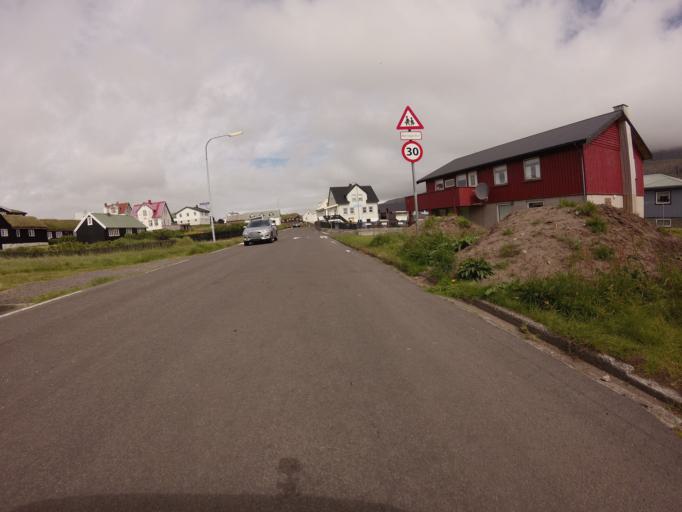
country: FO
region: Sandoy
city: Sandur
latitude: 61.8351
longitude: -6.8199
